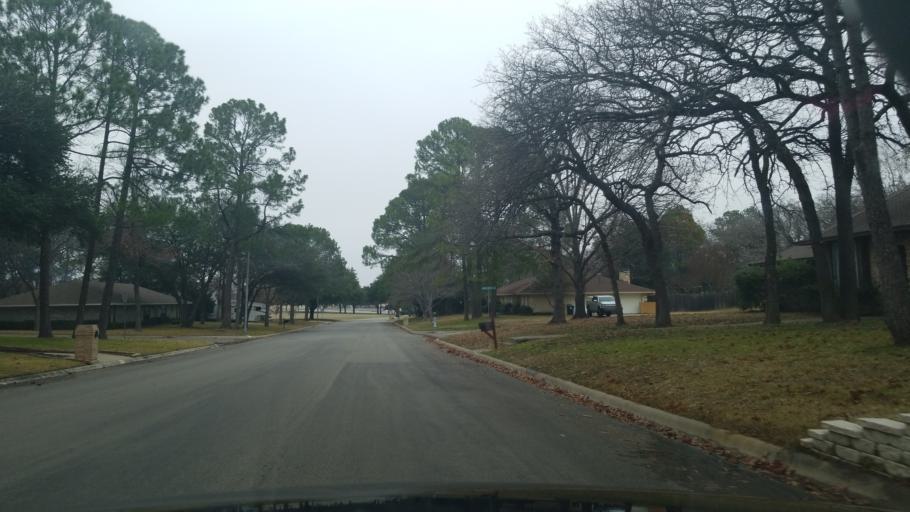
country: US
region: Texas
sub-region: Denton County
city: Denton
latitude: 33.1868
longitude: -97.1138
